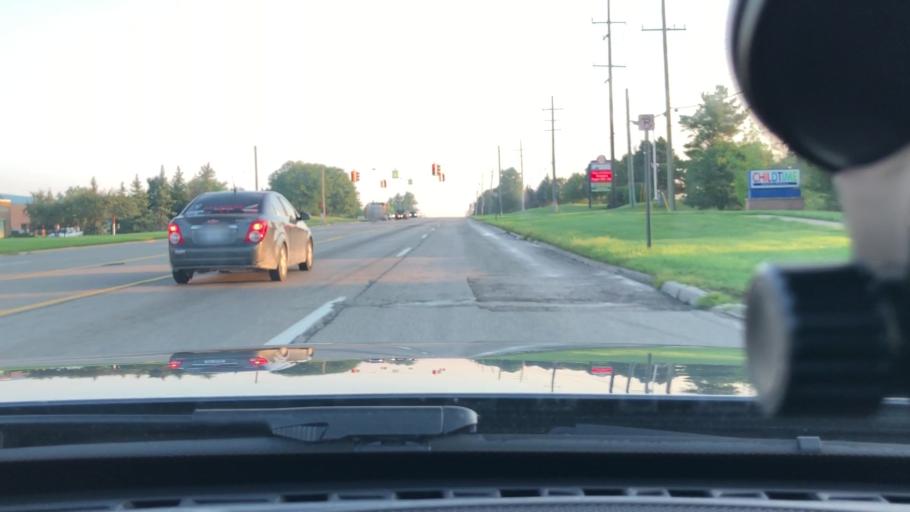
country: US
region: Michigan
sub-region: Wayne County
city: Plymouth
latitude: 42.3880
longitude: -83.5099
